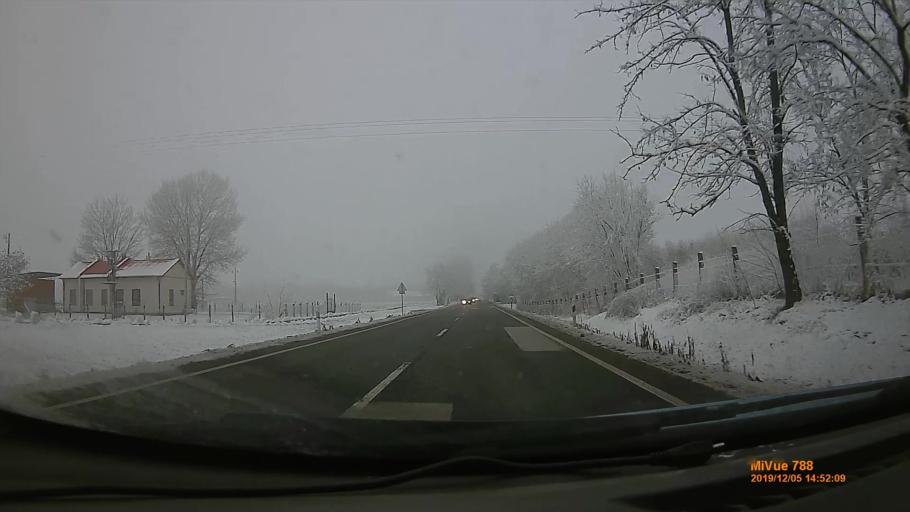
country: HU
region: Szabolcs-Szatmar-Bereg
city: Nyirtelek
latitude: 47.9987
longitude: 21.6482
